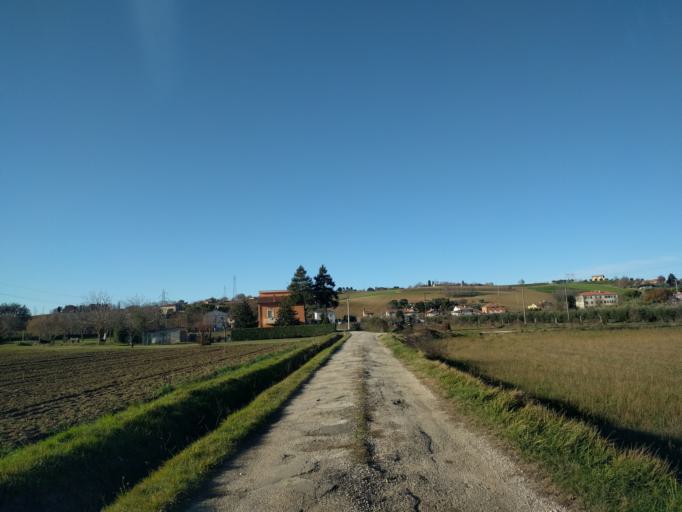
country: IT
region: The Marches
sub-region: Provincia di Pesaro e Urbino
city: Cuccurano
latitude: 43.7857
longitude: 12.9495
